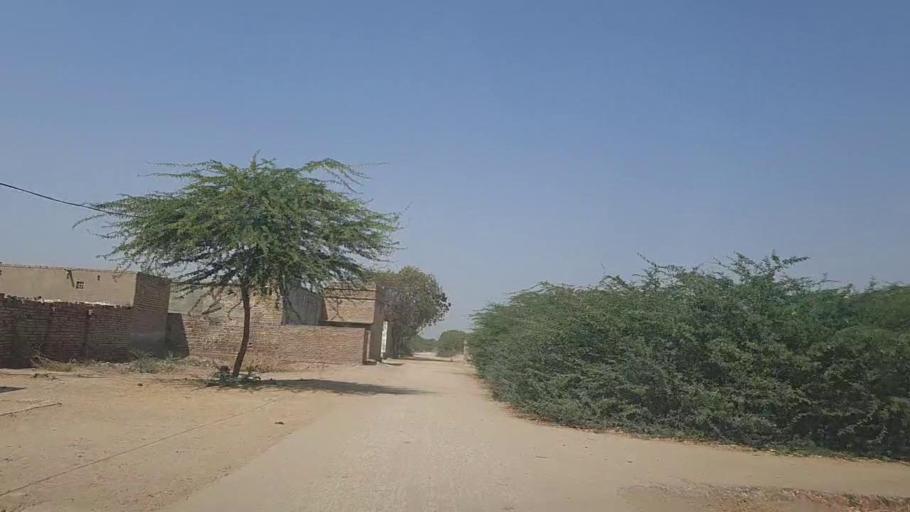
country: PK
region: Sindh
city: Naukot
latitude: 24.8480
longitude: 69.4395
